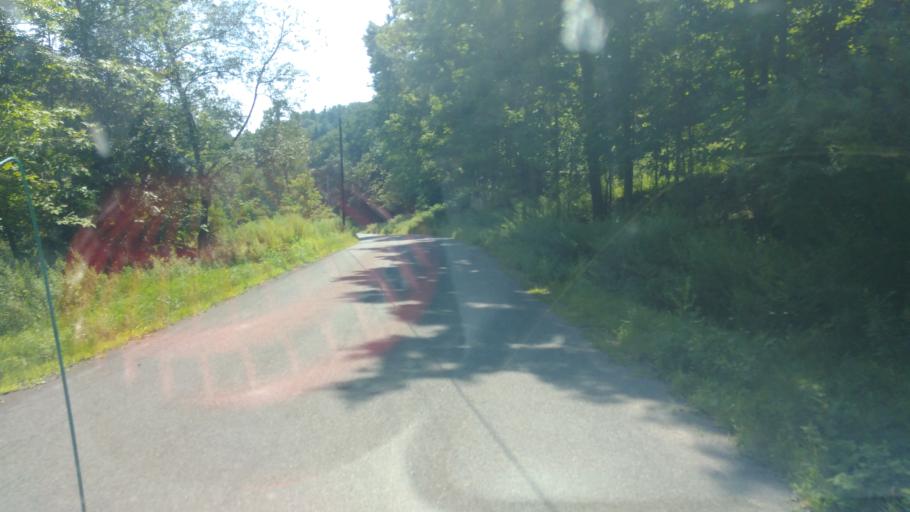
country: US
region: New York
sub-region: Steuben County
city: Canisteo
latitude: 42.2989
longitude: -77.6126
